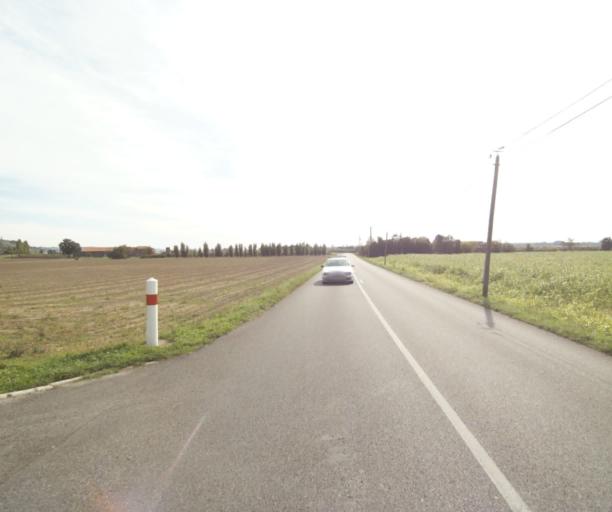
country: FR
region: Midi-Pyrenees
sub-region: Departement du Tarn-et-Garonne
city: Corbarieu
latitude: 43.9376
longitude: 1.3757
